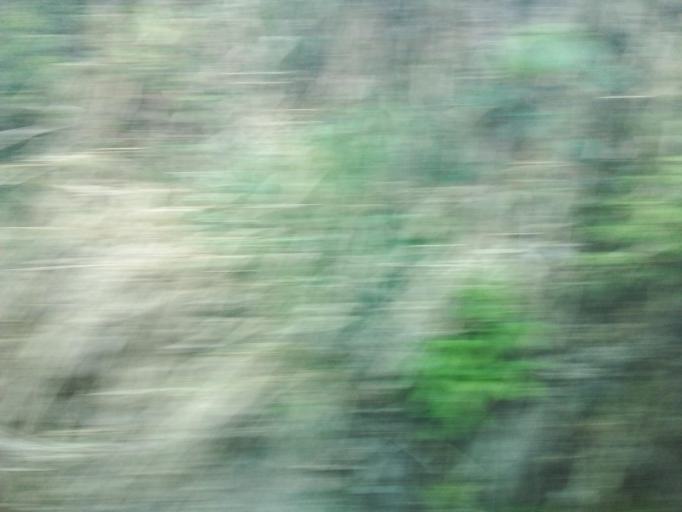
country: BR
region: Minas Gerais
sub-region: Timoteo
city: Timoteo
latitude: -19.5381
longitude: -42.6841
